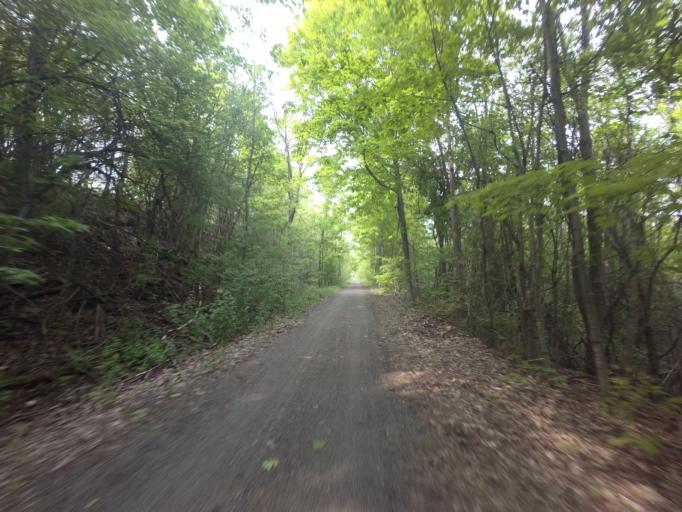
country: CA
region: Ontario
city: Kingston
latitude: 44.4112
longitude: -76.6282
